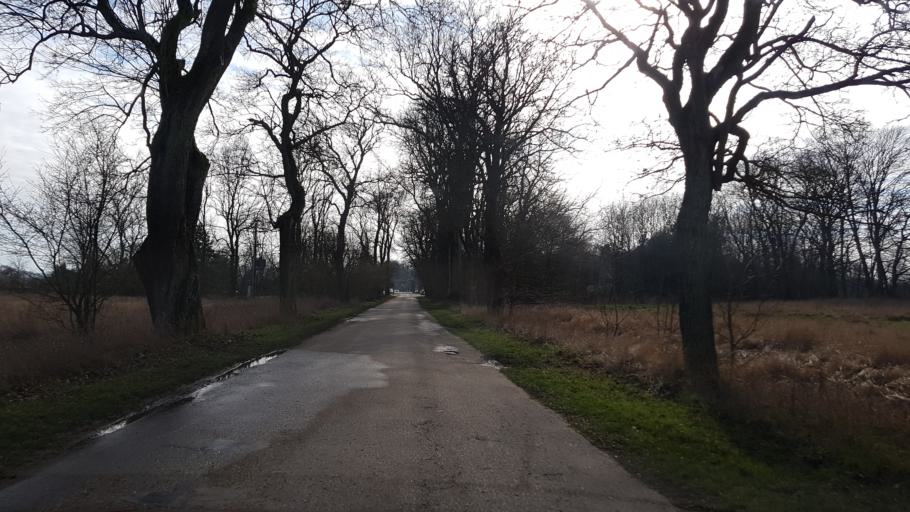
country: PL
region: West Pomeranian Voivodeship
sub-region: Powiat policki
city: Dobra
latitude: 53.5615
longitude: 14.3170
